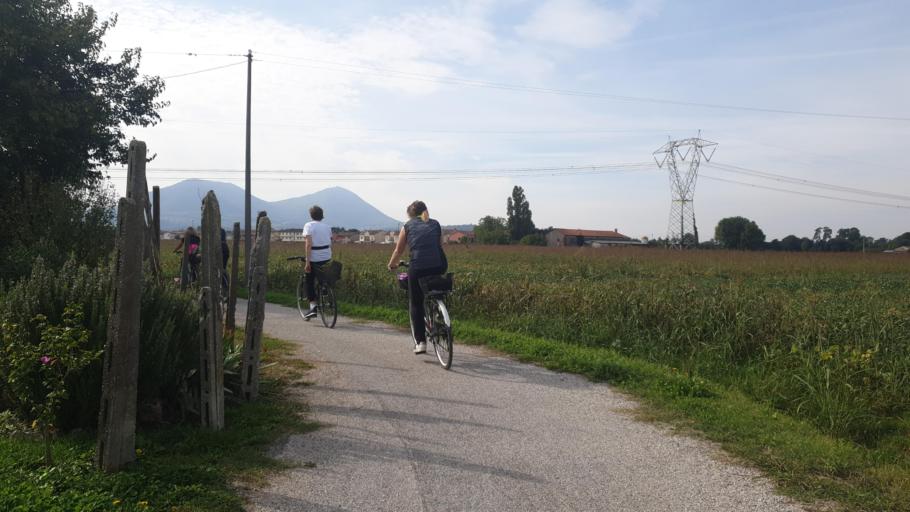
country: IT
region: Veneto
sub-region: Provincia di Padova
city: Cervarese Santa Croce
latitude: 45.4097
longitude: 11.6968
